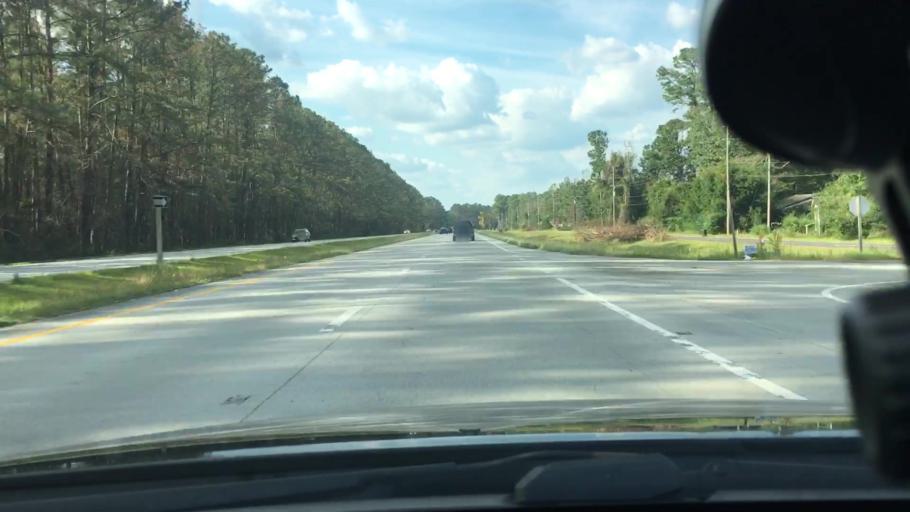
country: US
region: North Carolina
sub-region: Craven County
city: Neuse Forest
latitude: 34.9830
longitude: -76.9787
